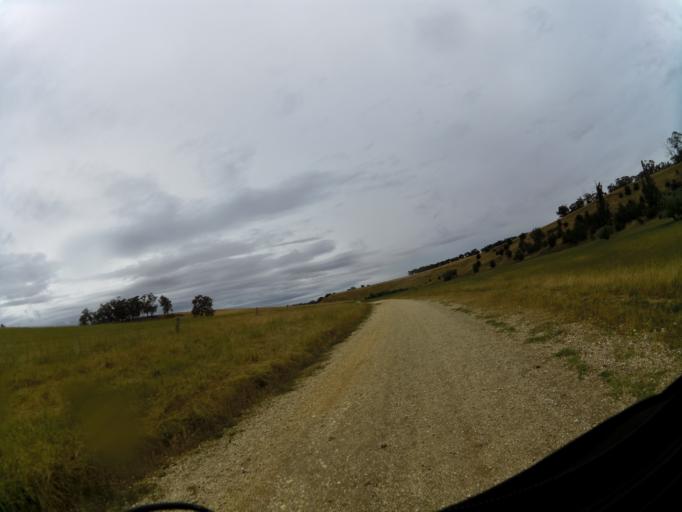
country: AU
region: Victoria
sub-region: Mount Alexander
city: Castlemaine
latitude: -37.2091
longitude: 144.0262
